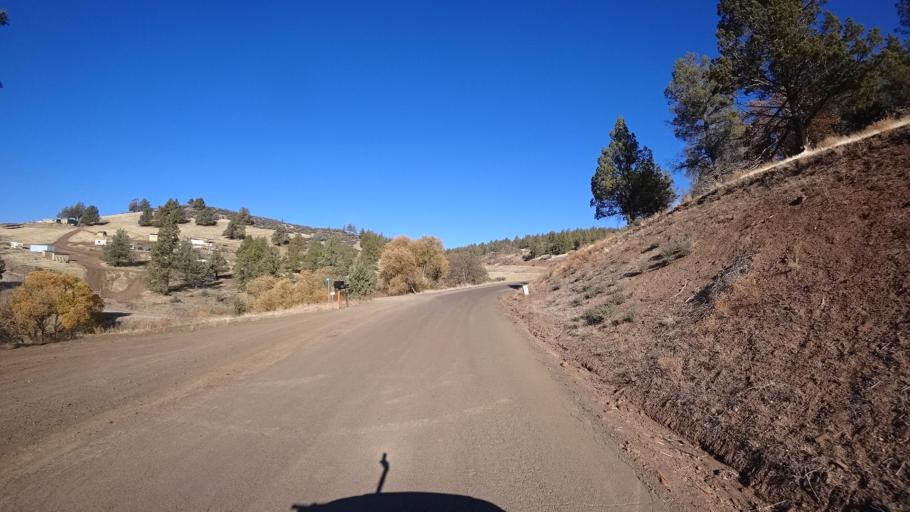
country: US
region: California
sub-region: Siskiyou County
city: Montague
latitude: 41.8991
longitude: -122.4242
